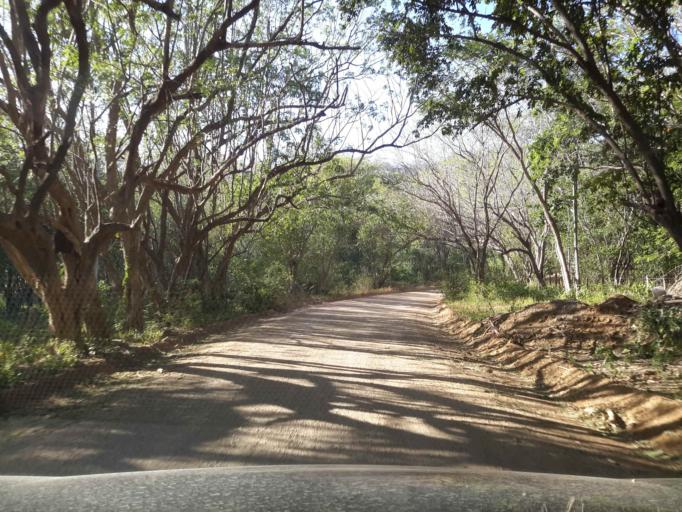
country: NI
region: Rivas
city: San Juan del Sur
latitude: 11.1770
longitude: -85.8021
